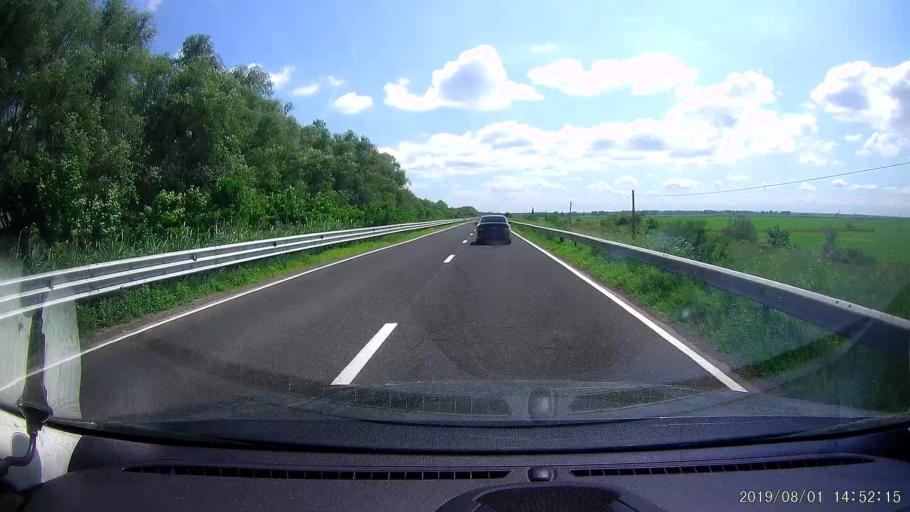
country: RO
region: Braila
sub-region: Comuna Vadeni
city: Vadeni
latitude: 45.3588
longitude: 28.0118
